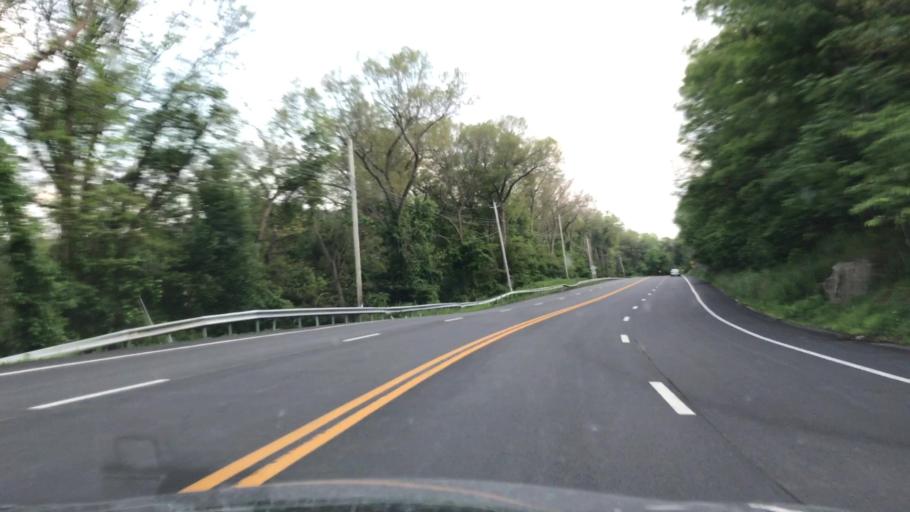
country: US
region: New York
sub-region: Orange County
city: Harriman
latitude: 41.2627
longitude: -74.1599
